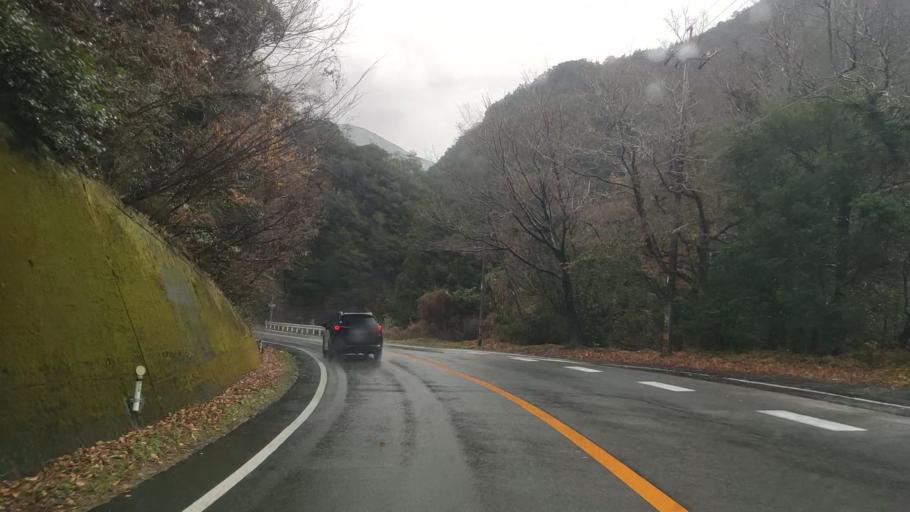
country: JP
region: Tokushima
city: Kamojimacho-jogejima
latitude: 34.1638
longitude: 134.3481
